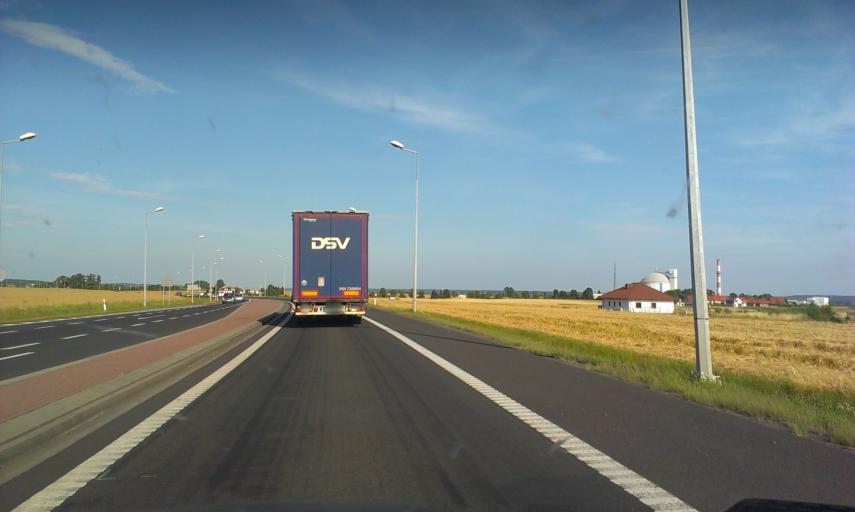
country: PL
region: Kujawsko-Pomorskie
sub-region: Powiat nakielski
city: Naklo nad Notecia
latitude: 53.1513
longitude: 17.6046
